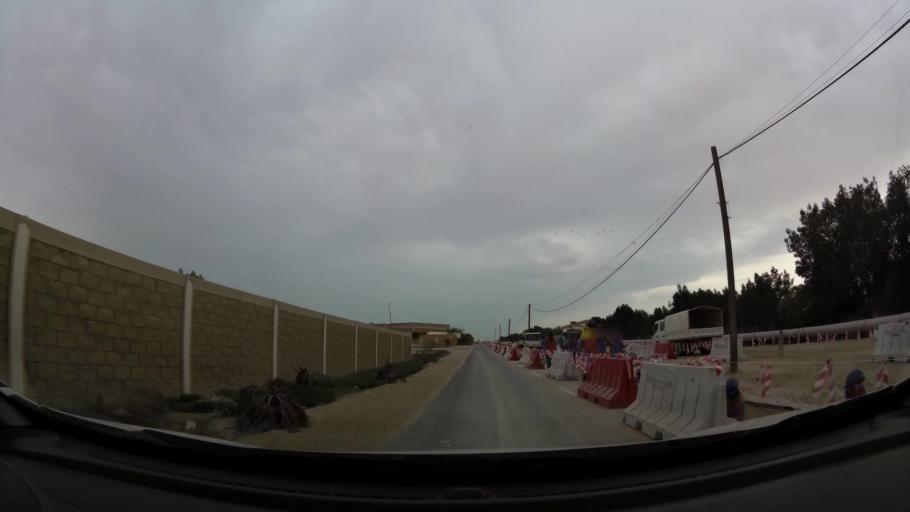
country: BH
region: Central Governorate
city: Madinat Hamad
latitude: 26.1439
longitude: 50.4748
